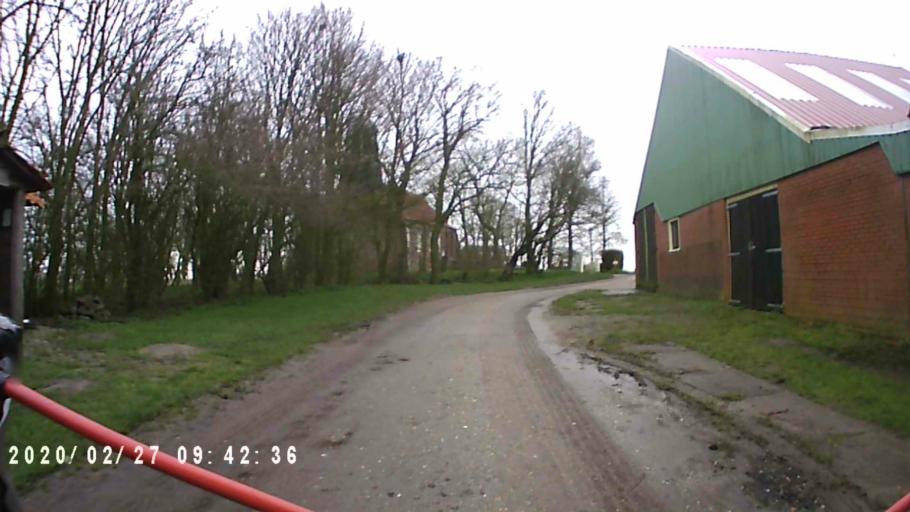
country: NL
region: Groningen
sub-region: Gemeente Zuidhorn
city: Aduard
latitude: 53.2780
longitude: 6.4467
